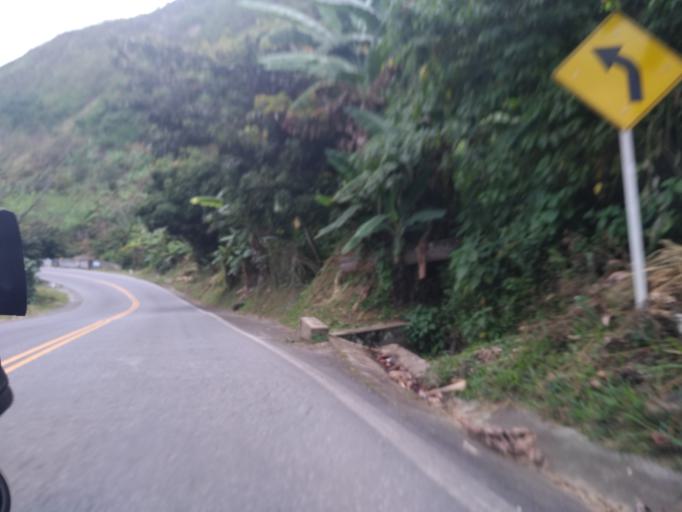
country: CO
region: Cauca
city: Rosas
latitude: 2.2506
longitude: -76.7645
